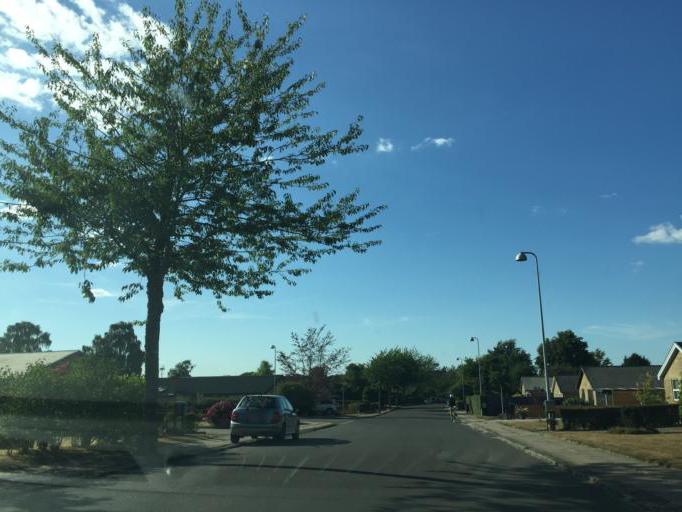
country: DK
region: South Denmark
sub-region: Odense Kommune
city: Odense
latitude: 55.3718
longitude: 10.3537
